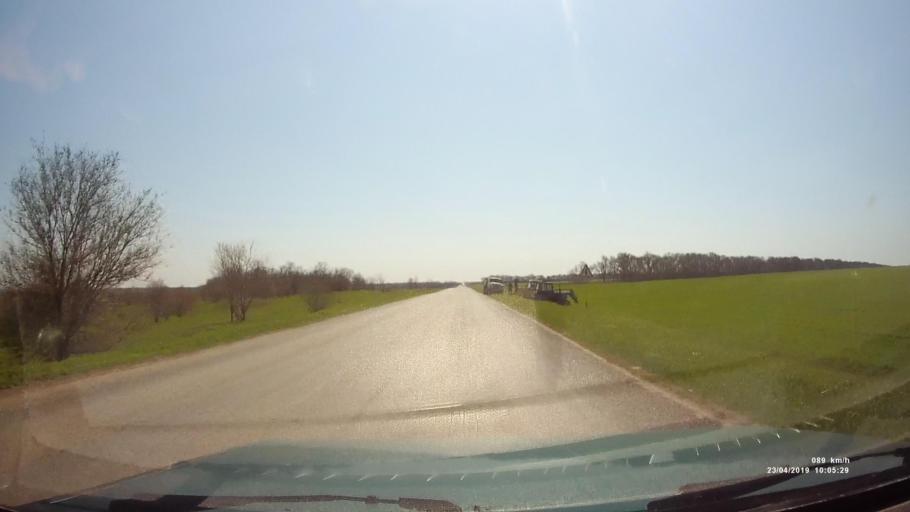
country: RU
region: Rostov
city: Sovetskoye
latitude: 46.7408
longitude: 42.2204
